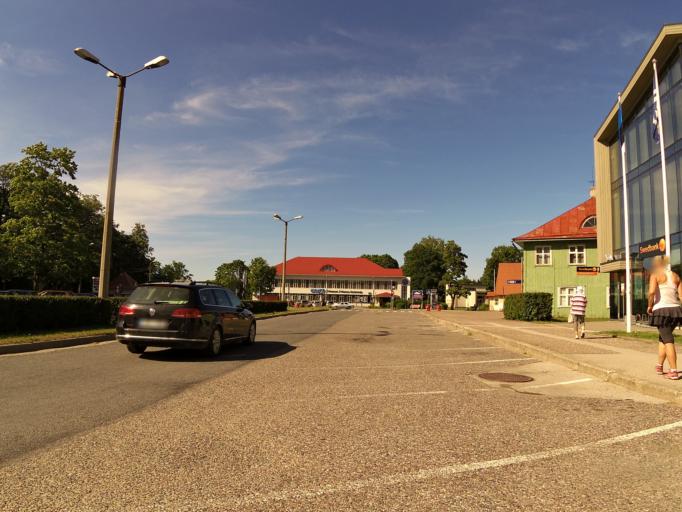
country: EE
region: Hiiumaa
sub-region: Kaerdla linn
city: Kardla
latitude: 58.9974
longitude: 22.7471
